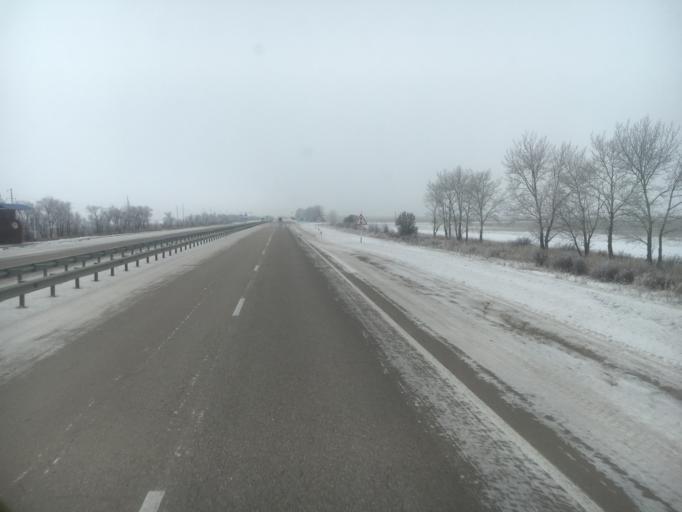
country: KZ
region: Aqmola
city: Akkol'
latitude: 53.3412
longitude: 69.5083
